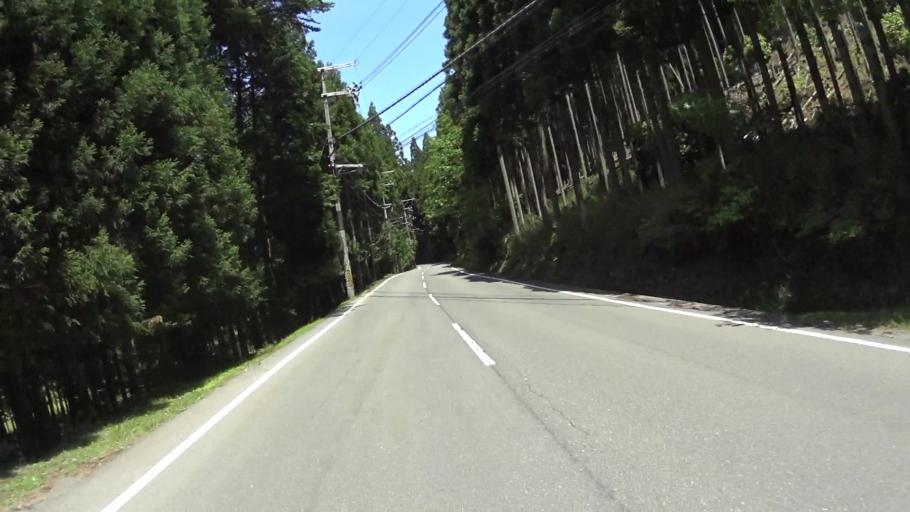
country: JP
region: Kyoto
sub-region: Kyoto-shi
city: Kamigyo-ku
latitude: 35.1919
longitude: 135.7059
